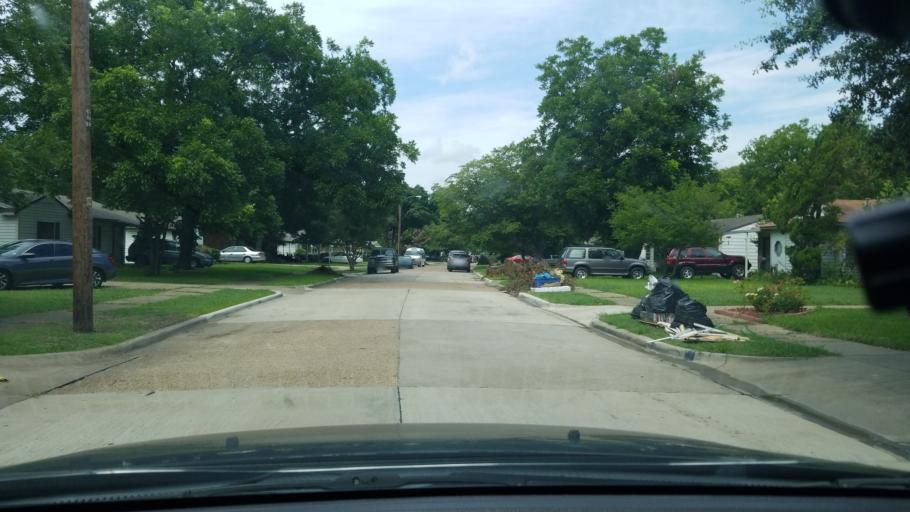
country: US
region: Texas
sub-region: Dallas County
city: Garland
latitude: 32.8253
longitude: -96.6726
